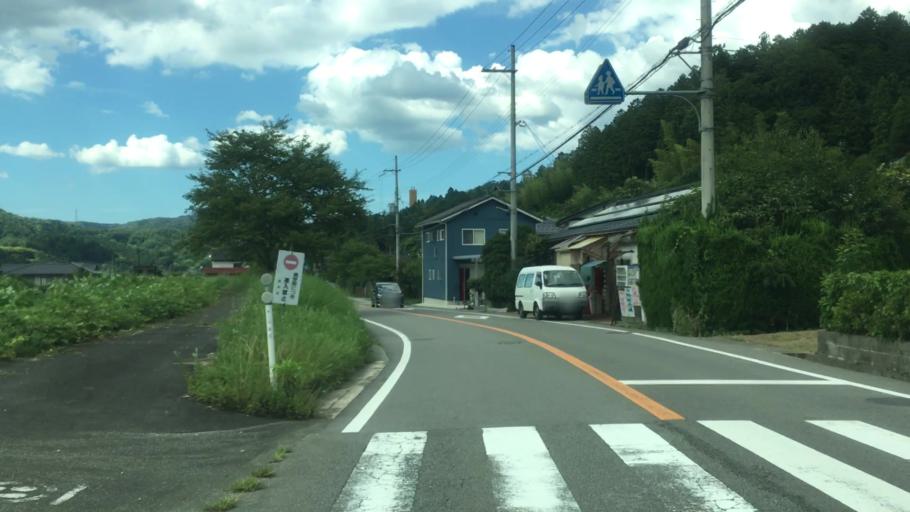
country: JP
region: Hyogo
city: Toyooka
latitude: 35.5400
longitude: 134.7902
